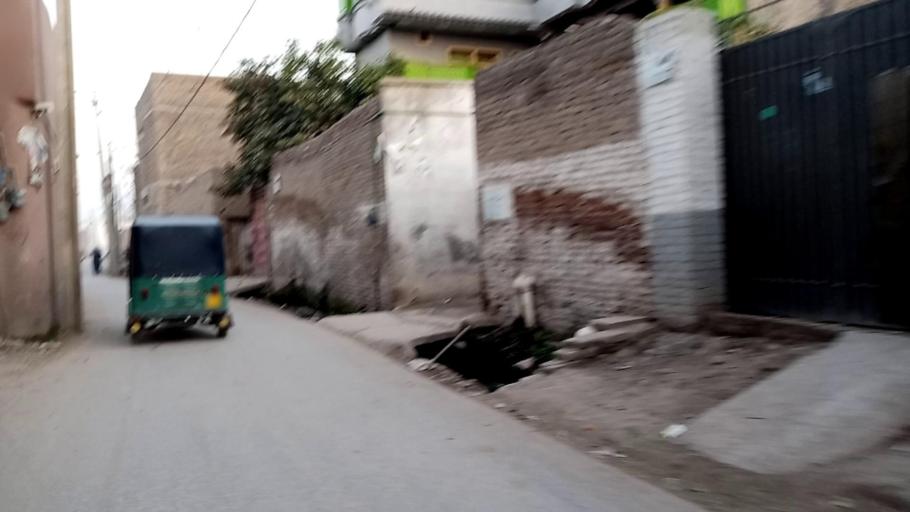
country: PK
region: Khyber Pakhtunkhwa
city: Peshawar
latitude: 34.0316
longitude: 71.4929
